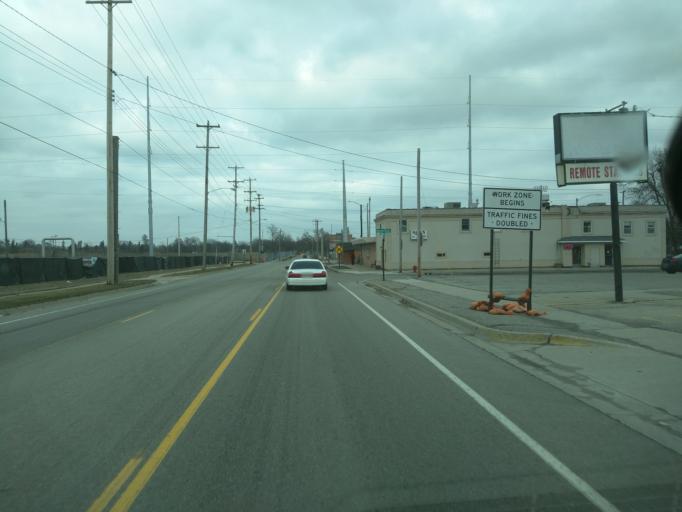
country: US
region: Michigan
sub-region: Ingham County
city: Edgemont Park
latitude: 42.7338
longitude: -84.5838
